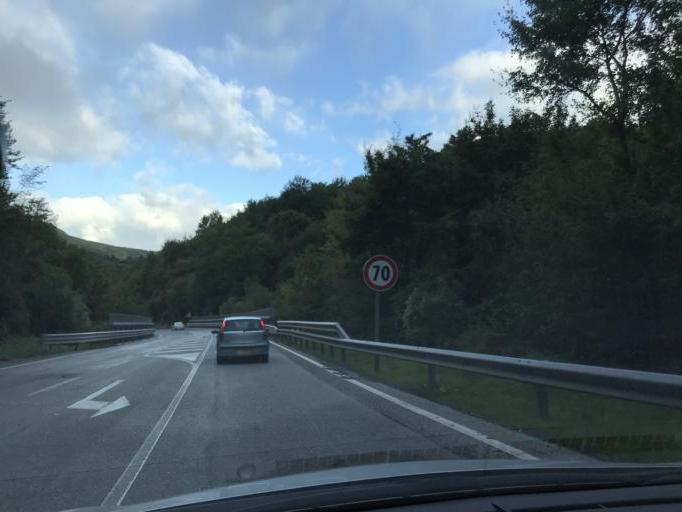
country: IT
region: Umbria
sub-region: Provincia di Terni
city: Ferentillo
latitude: 42.6684
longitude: 12.7336
